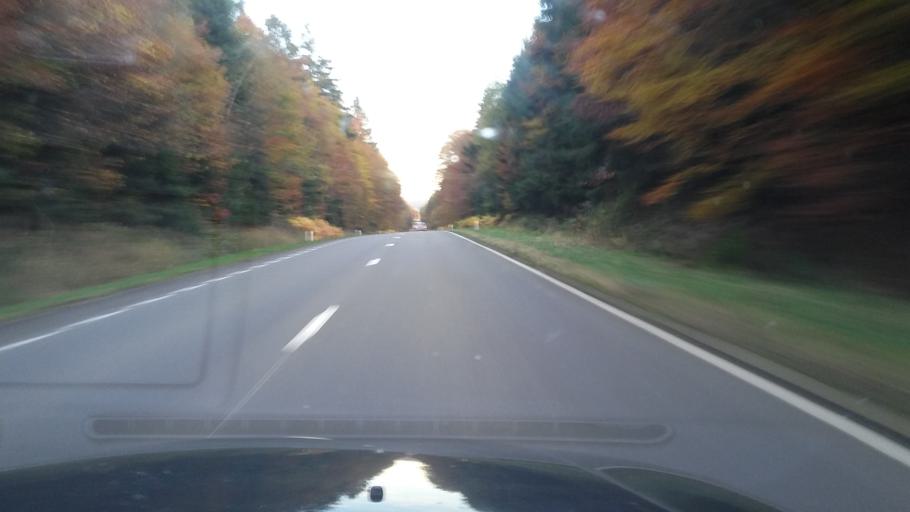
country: BE
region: Wallonia
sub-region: Province du Luxembourg
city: Herbeumont
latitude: 49.7494
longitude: 5.2101
